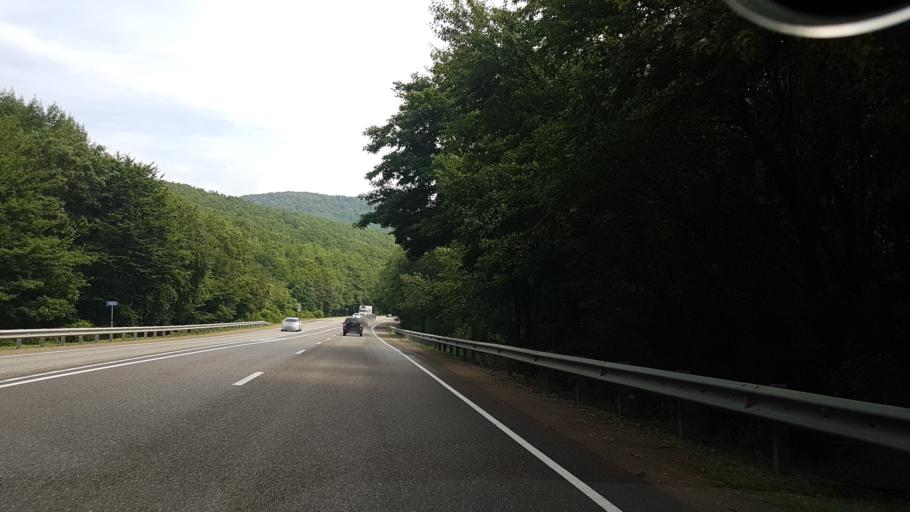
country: RU
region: Krasnodarskiy
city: Goryachiy Klyuch
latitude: 44.5221
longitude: 38.9306
